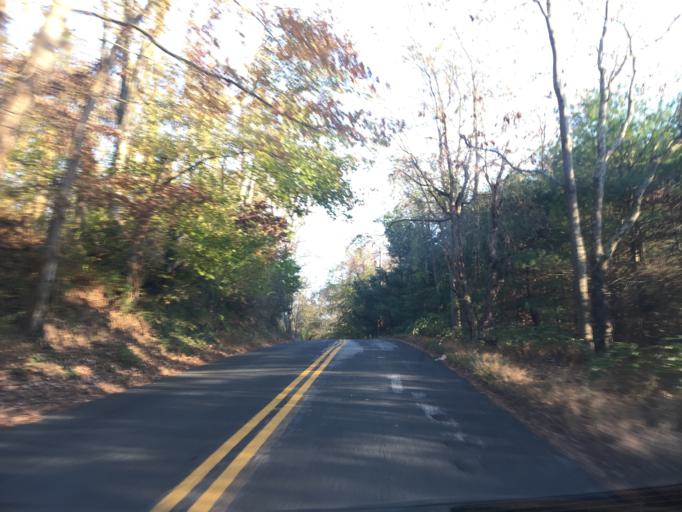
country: US
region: Maryland
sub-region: Baltimore County
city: Hampton
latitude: 39.4735
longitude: -76.5325
